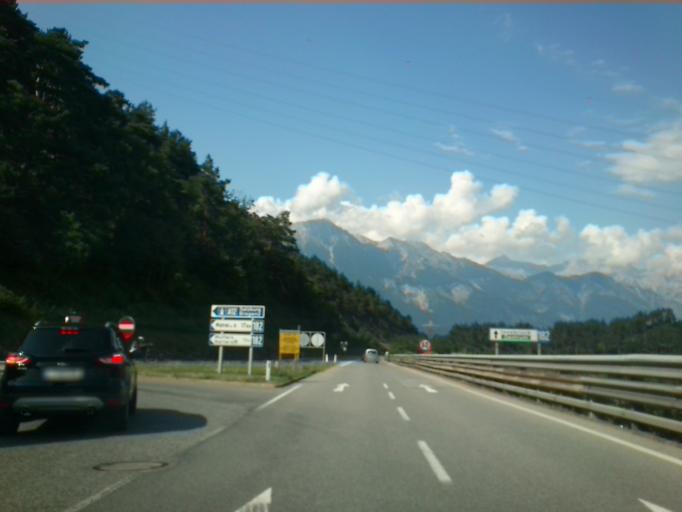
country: AT
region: Tyrol
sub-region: Politischer Bezirk Innsbruck Land
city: Mutters
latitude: 47.2418
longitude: 11.3902
